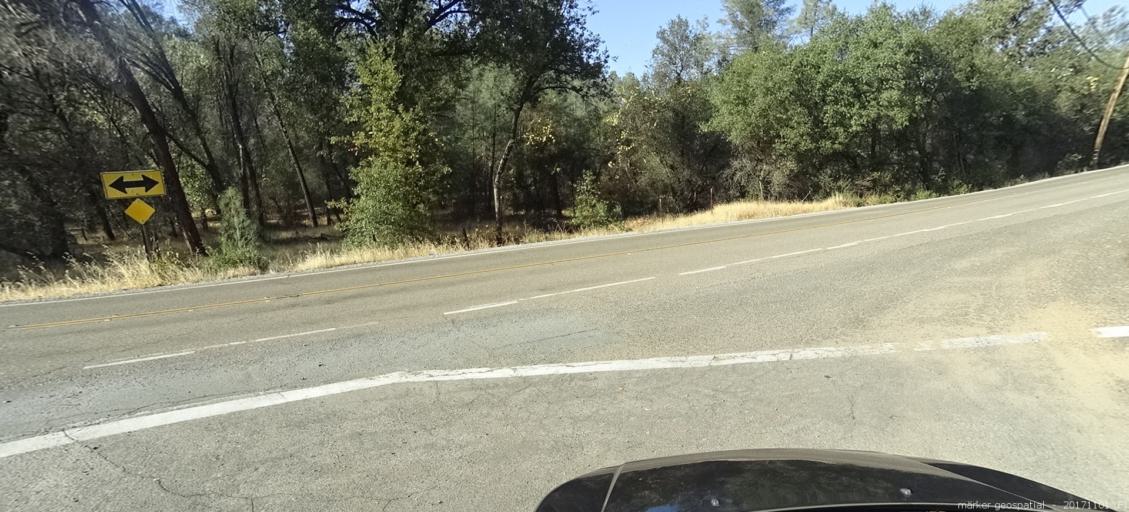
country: US
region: California
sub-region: Shasta County
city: Shasta Lake
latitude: 40.6775
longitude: -122.3020
